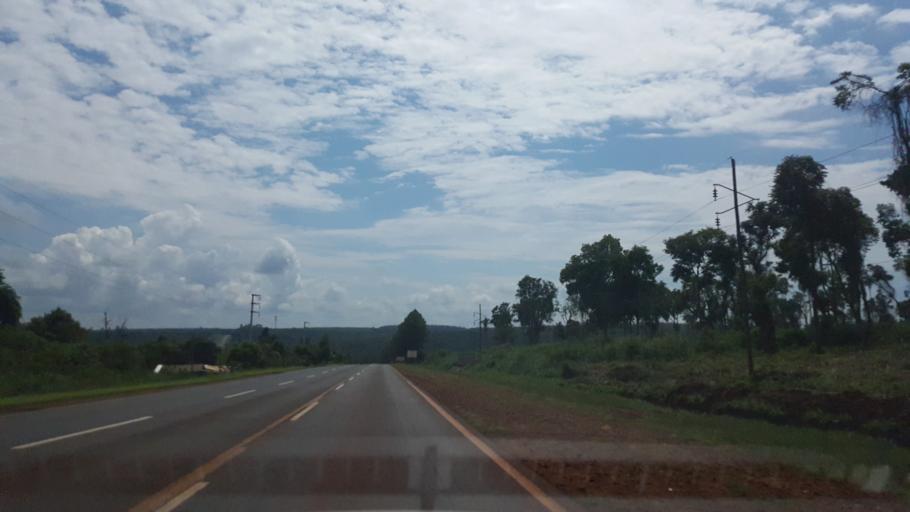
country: AR
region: Misiones
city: Capiovi
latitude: -26.8705
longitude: -55.0472
